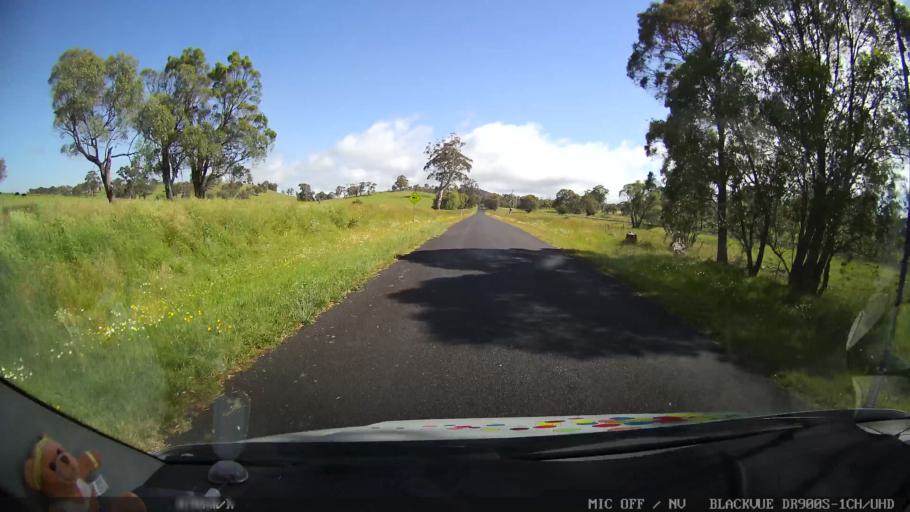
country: AU
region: New South Wales
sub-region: Guyra
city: Guyra
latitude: -30.0448
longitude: 151.6671
